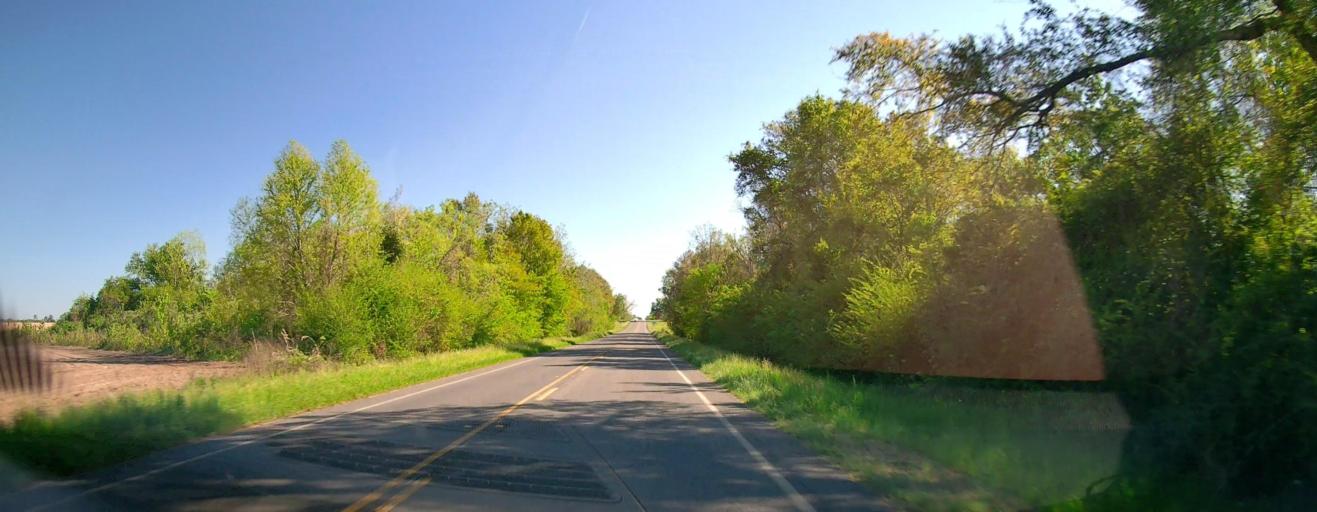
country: US
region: Georgia
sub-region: Wilcox County
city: Rochelle
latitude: 31.9637
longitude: -83.4563
